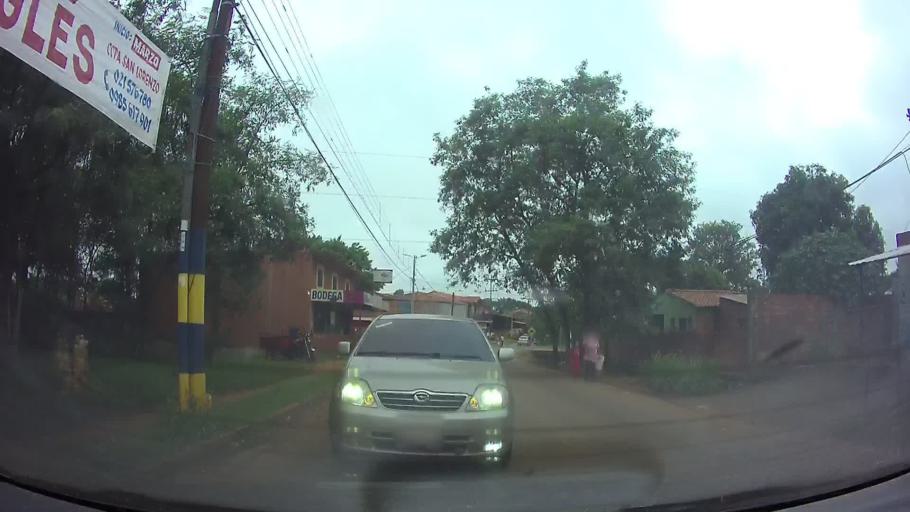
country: PY
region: Central
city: San Lorenzo
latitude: -25.3128
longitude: -57.4925
